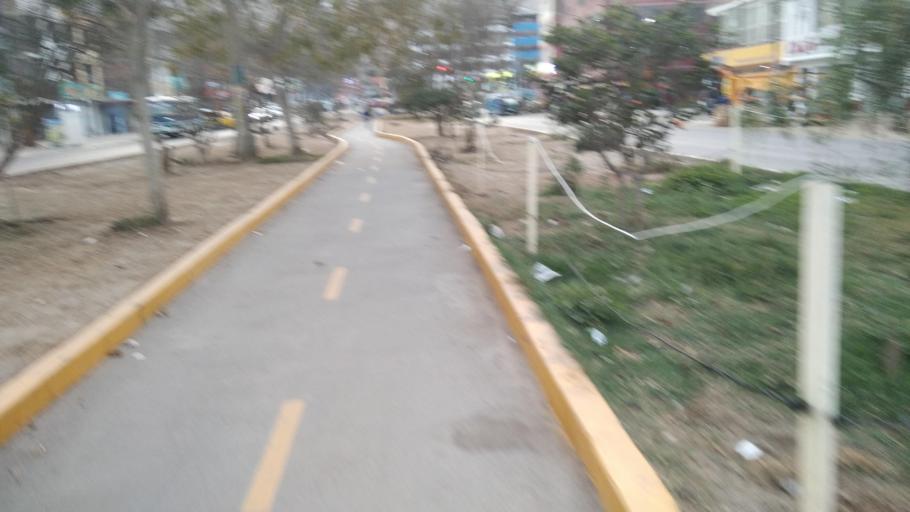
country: PE
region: Lima
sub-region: Lima
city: Independencia
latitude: -11.9898
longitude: -77.0141
